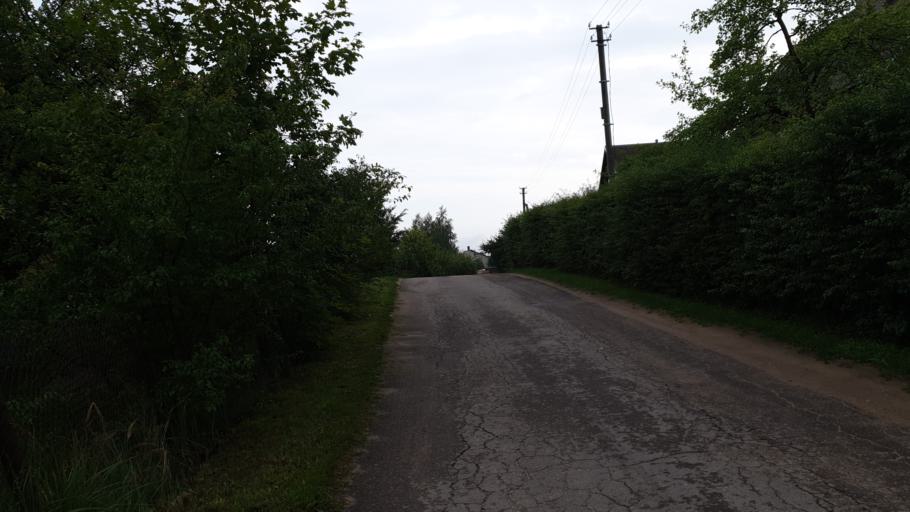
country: LT
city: Grigiskes
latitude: 54.7702
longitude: 25.0171
